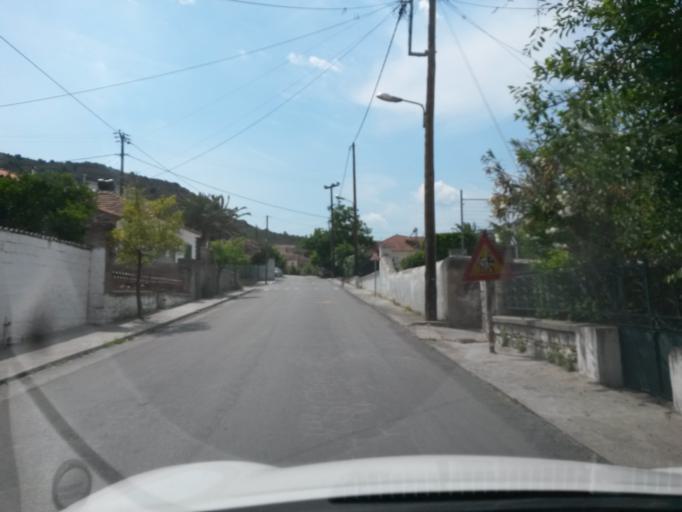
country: GR
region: North Aegean
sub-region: Nomos Lesvou
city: Kalloni
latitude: 39.2425
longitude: 26.2002
